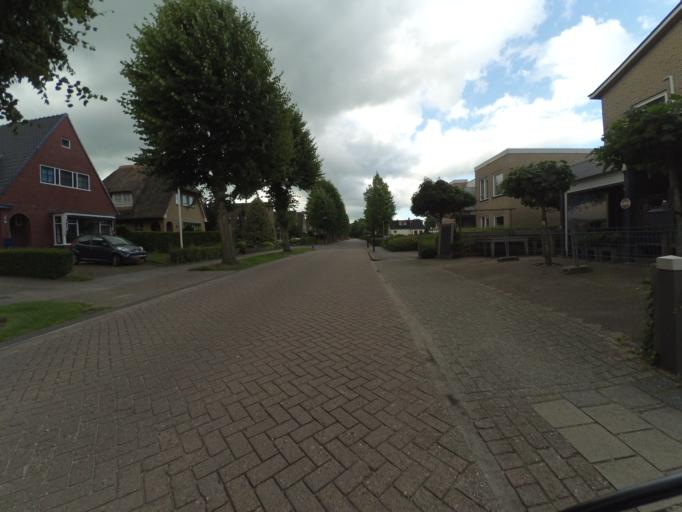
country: NL
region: Friesland
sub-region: Gemeente Tytsjerksteradiel
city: Hurdegaryp
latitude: 53.2167
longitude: 5.9416
